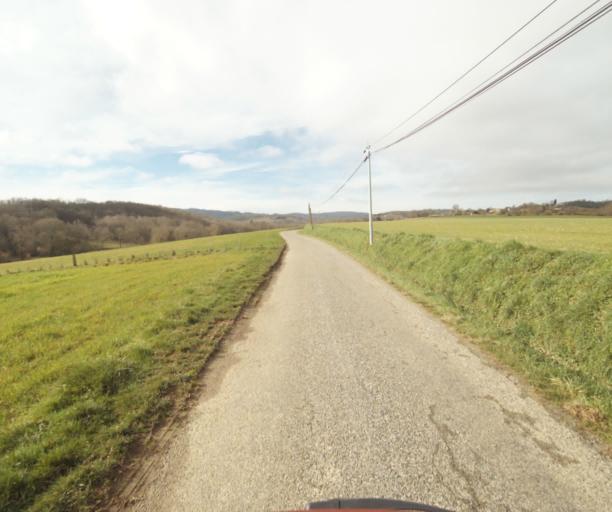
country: FR
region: Midi-Pyrenees
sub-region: Departement de l'Ariege
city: Pamiers
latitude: 43.1037
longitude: 1.5322
